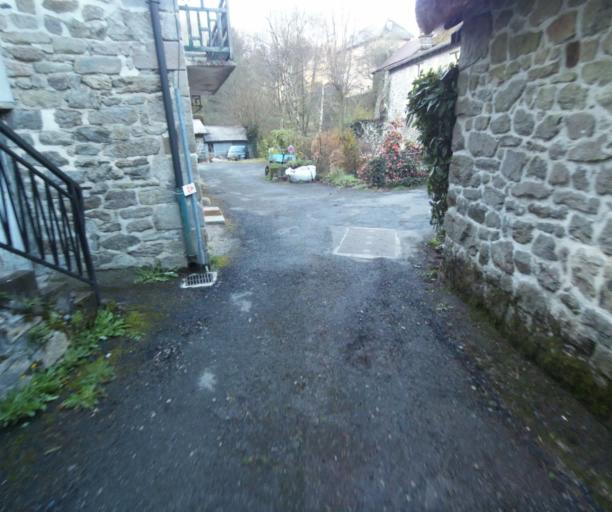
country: FR
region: Limousin
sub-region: Departement de la Correze
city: Correze
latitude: 45.2998
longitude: 1.8517
